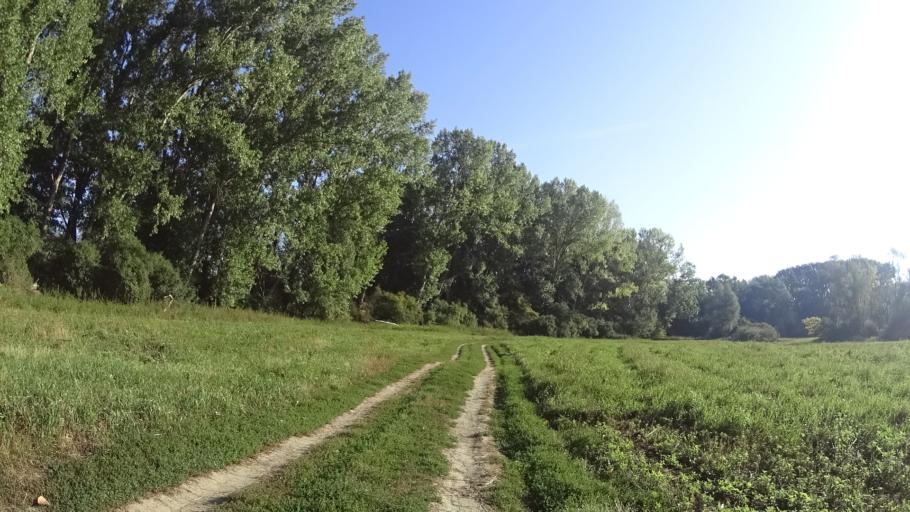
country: AT
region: Lower Austria
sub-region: Politischer Bezirk Mistelbach
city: Rabensburg
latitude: 48.6181
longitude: 16.9437
